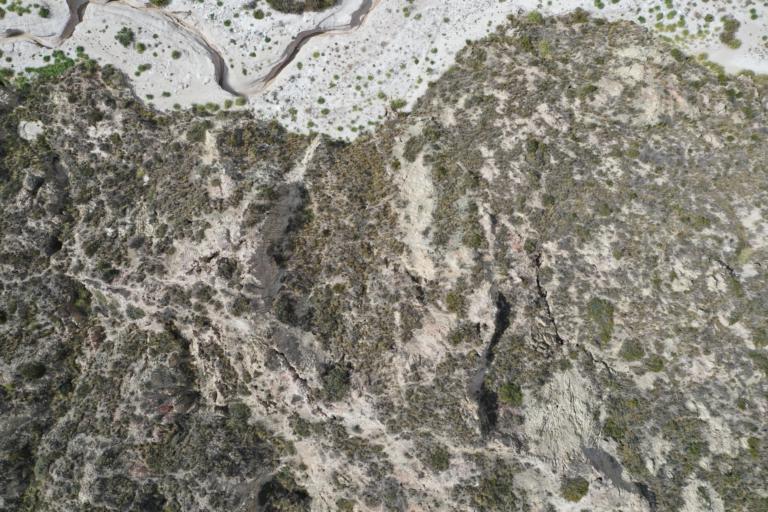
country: BO
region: La Paz
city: La Paz
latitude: -16.5635
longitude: -68.1228
